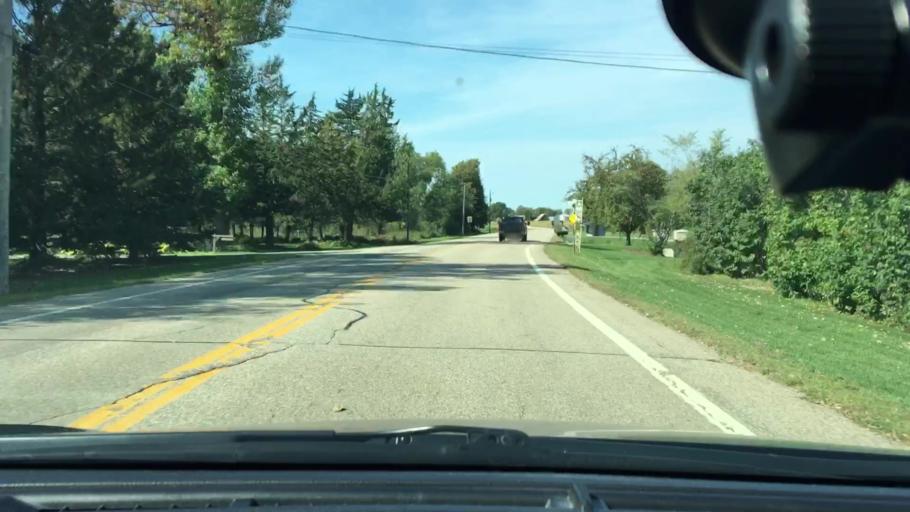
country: US
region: Minnesota
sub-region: Wright County
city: Hanover
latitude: 45.1228
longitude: -93.6164
